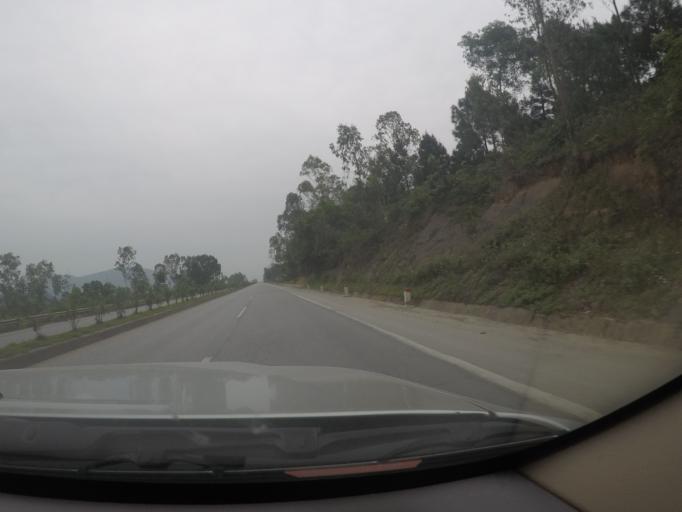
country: VN
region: Nghe An
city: Quan Hanh
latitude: 18.8667
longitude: 105.6276
